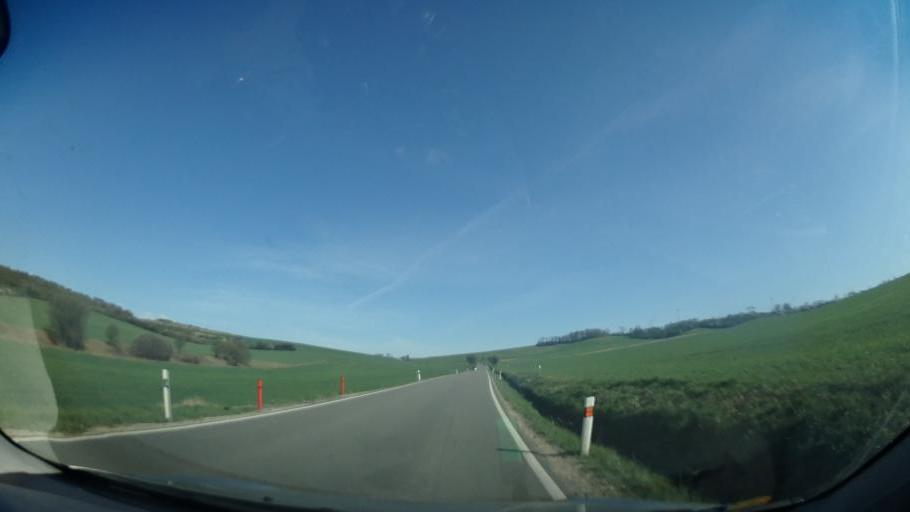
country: CZ
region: South Moravian
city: Ostopovice
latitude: 49.1538
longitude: 16.5557
